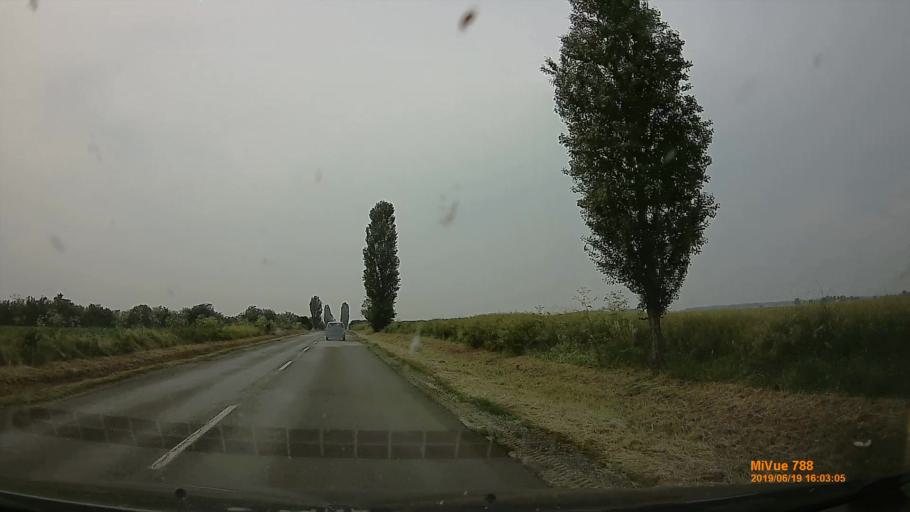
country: HU
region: Baranya
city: Szigetvar
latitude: 46.0649
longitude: 17.7717
